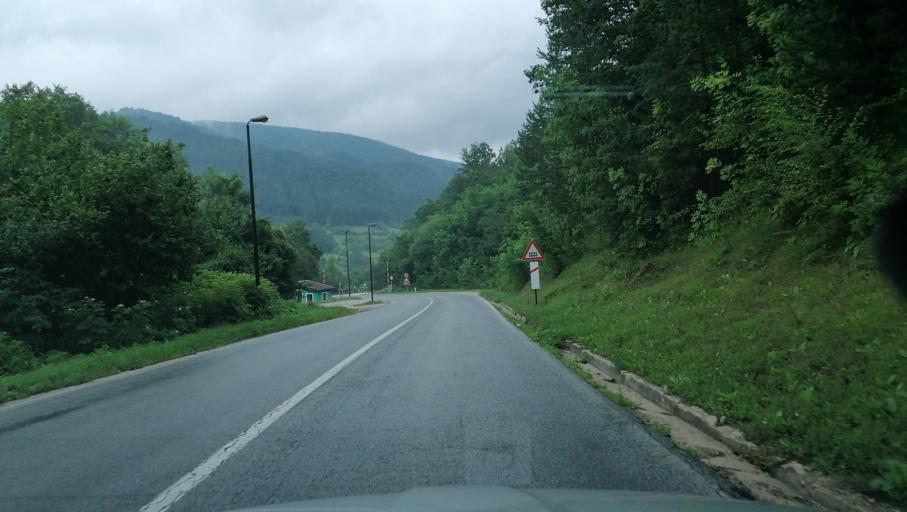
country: RS
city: Durici
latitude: 43.7966
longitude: 19.5109
